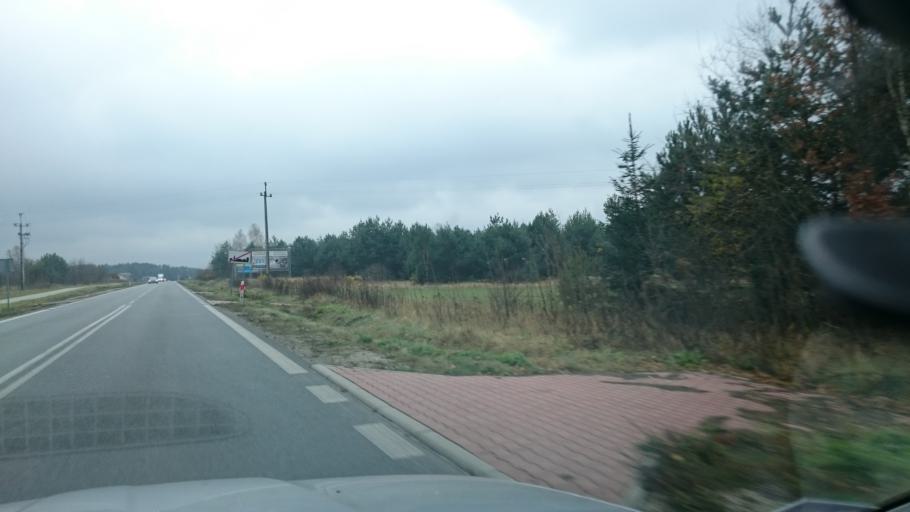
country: PL
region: Swietokrzyskie
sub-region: Powiat konecki
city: Konskie
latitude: 51.1341
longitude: 20.3621
